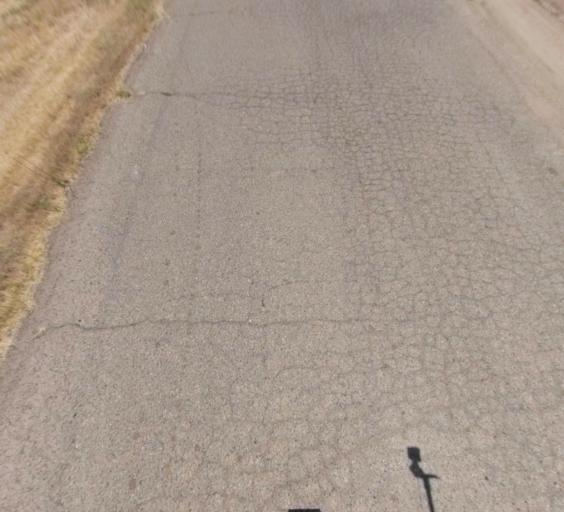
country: US
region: California
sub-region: Madera County
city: Parksdale
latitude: 36.9272
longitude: -119.9471
